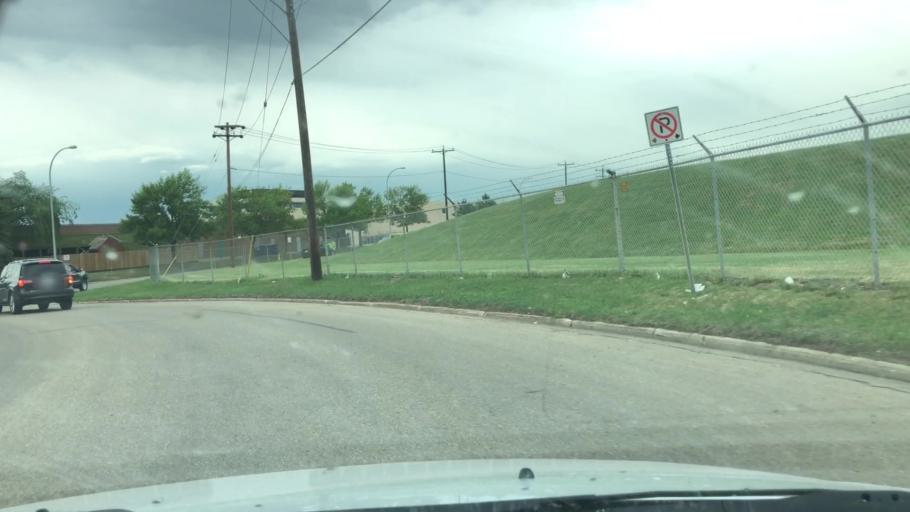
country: CA
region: Alberta
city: Edmonton
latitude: 53.5372
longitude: -113.4142
